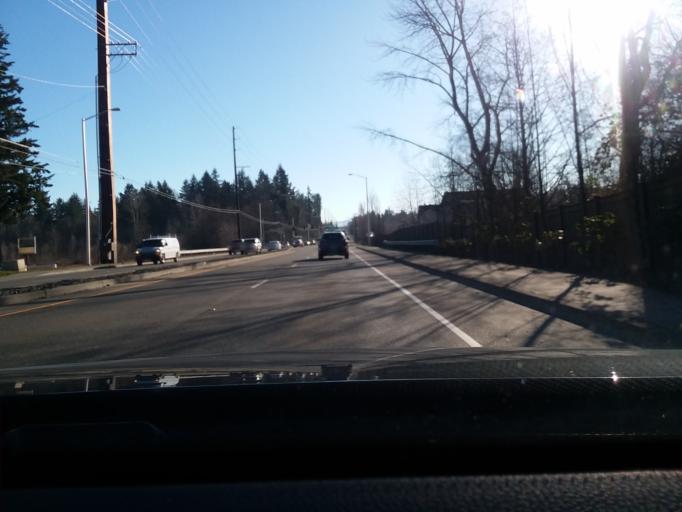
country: US
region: Washington
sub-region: Pierce County
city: Frederickson
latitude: 47.0965
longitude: -122.3386
